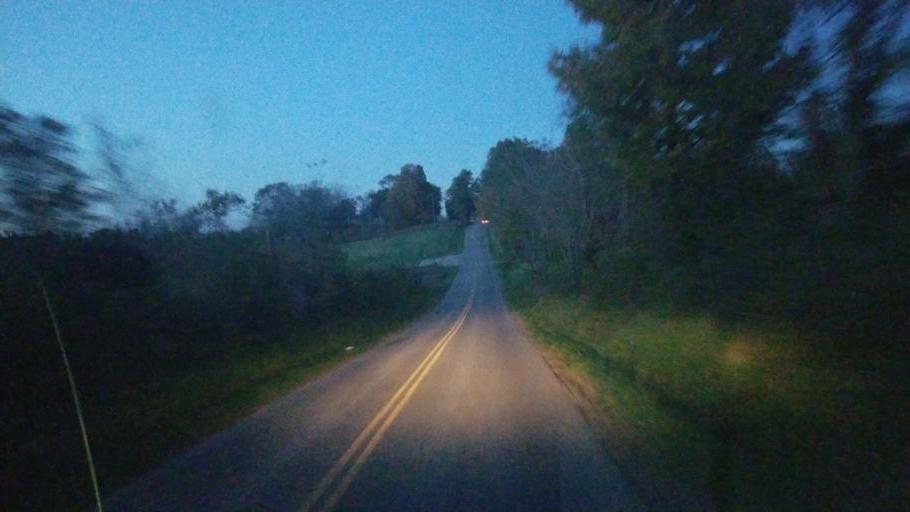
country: US
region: Ohio
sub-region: Perry County
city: Somerset
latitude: 39.8684
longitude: -82.2262
